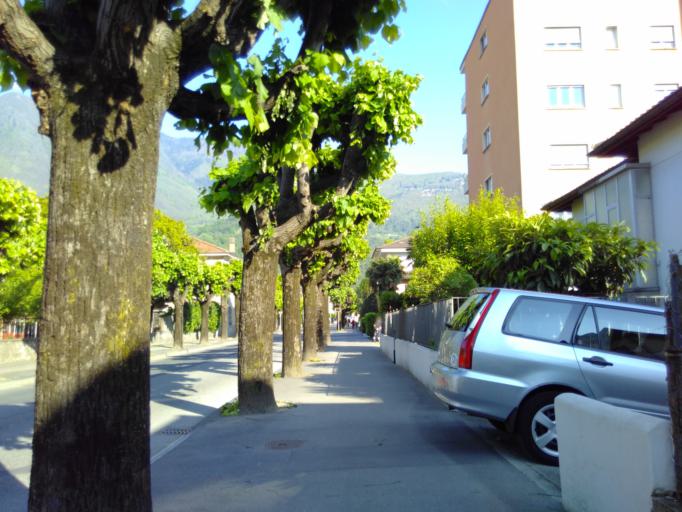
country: CH
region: Ticino
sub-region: Bellinzona District
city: Bellinzona
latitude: 46.1920
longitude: 9.0146
